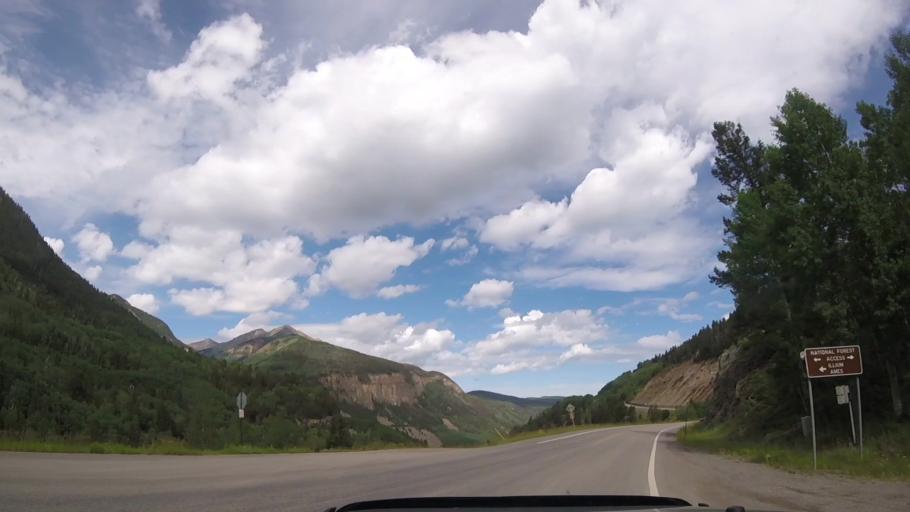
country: US
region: Colorado
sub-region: San Miguel County
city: Mountain Village
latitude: 37.8621
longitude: -107.8703
